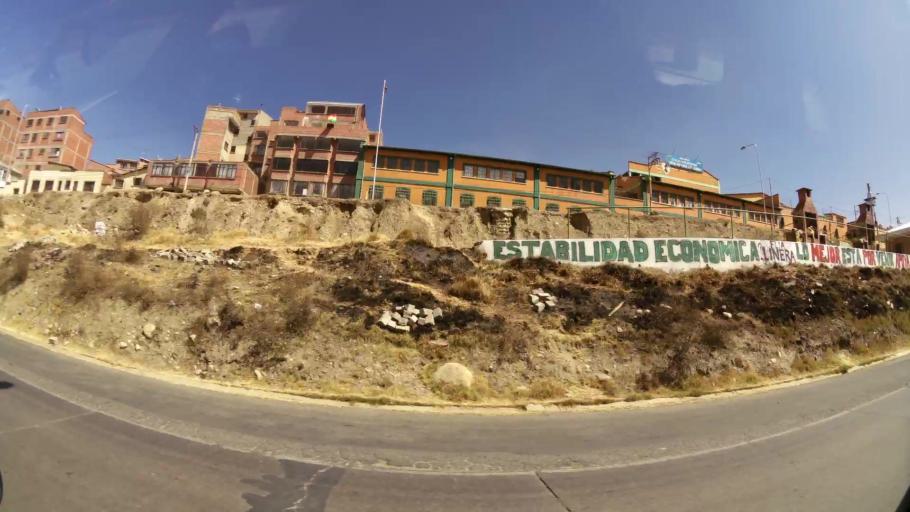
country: BO
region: La Paz
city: La Paz
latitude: -16.4831
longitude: -68.1475
